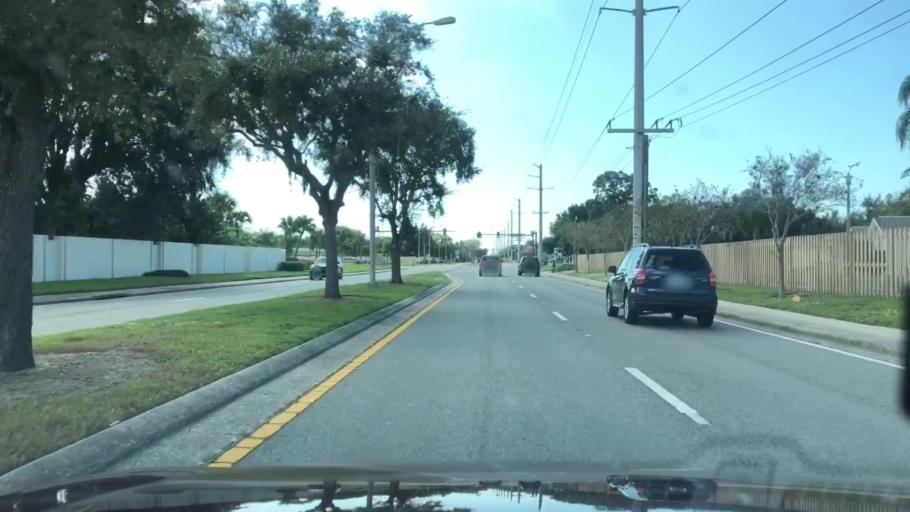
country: US
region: Florida
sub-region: Sarasota County
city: Gulf Gate Estates
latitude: 27.2575
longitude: -82.4977
